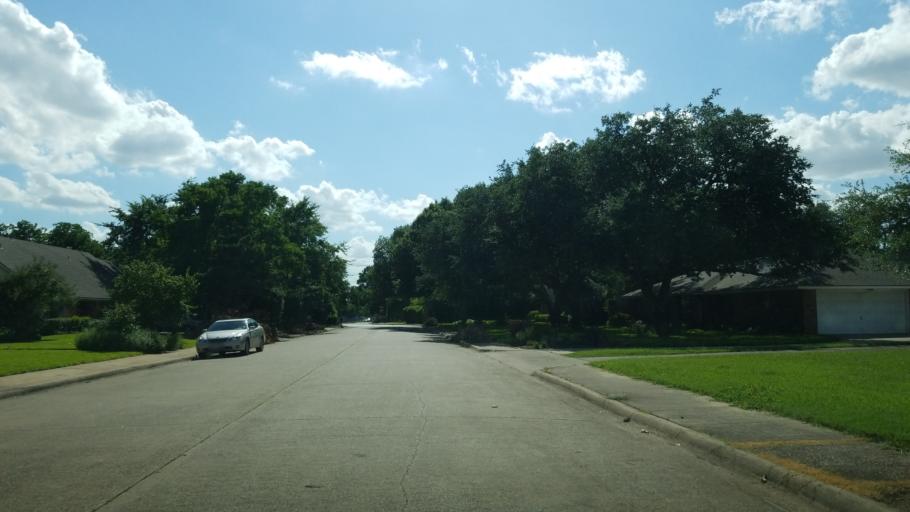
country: US
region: Texas
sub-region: Dallas County
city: University Park
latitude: 32.8836
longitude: -96.8416
